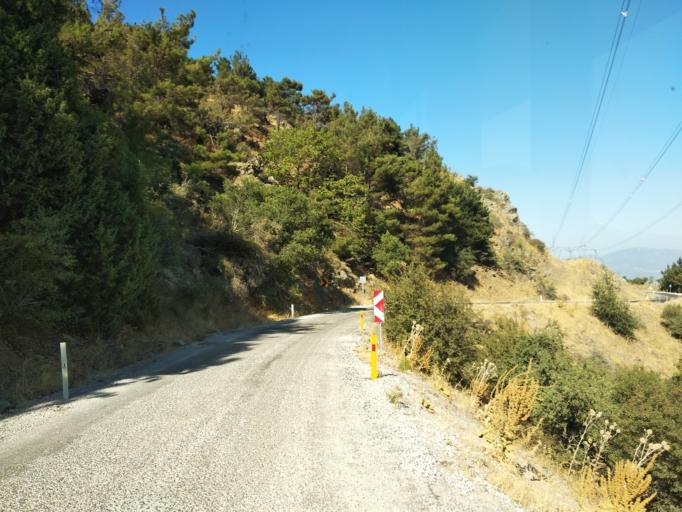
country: TR
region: Izmir
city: Gaziemir
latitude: 38.3150
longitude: 27.0066
